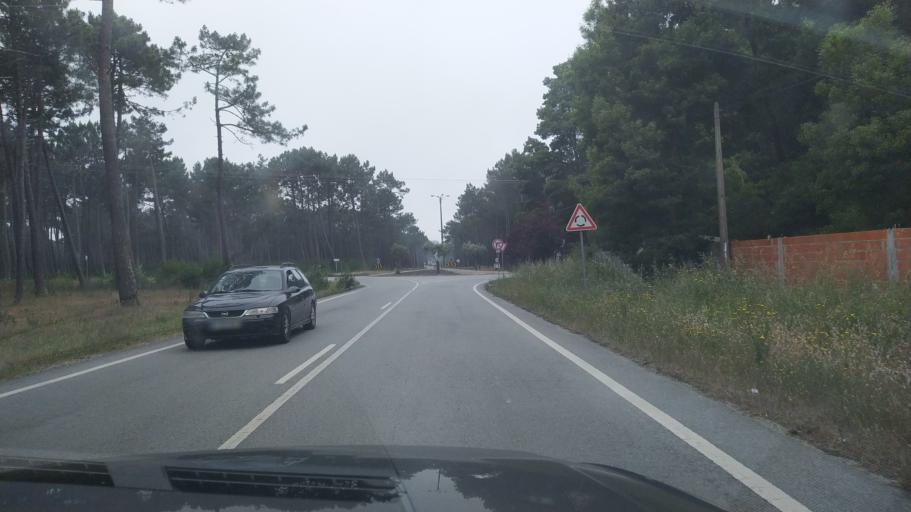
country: PT
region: Aveiro
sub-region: Ilhavo
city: Gafanha da Encarnacao
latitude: 40.5870
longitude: -8.7295
